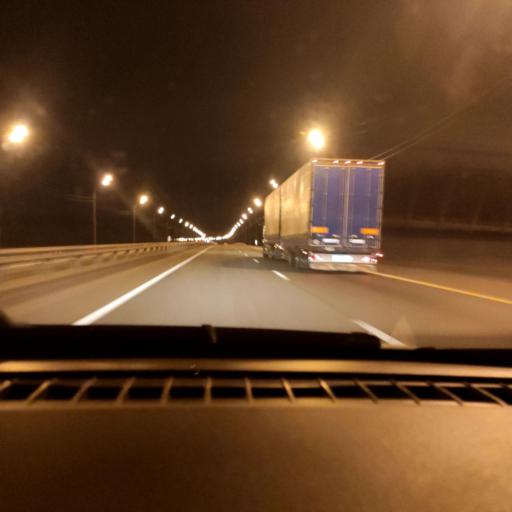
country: RU
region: Lipetsk
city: Khlevnoye
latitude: 52.2731
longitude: 39.0566
